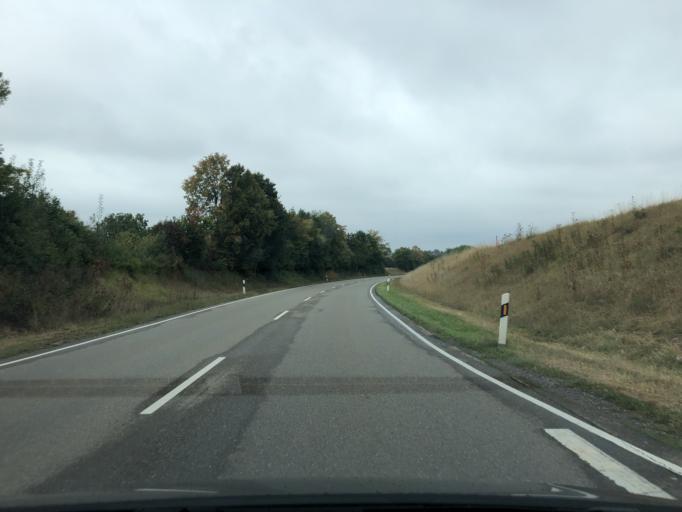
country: DE
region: Baden-Wuerttemberg
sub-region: Regierungsbezirk Stuttgart
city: Bondorf
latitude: 48.5513
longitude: 8.8438
